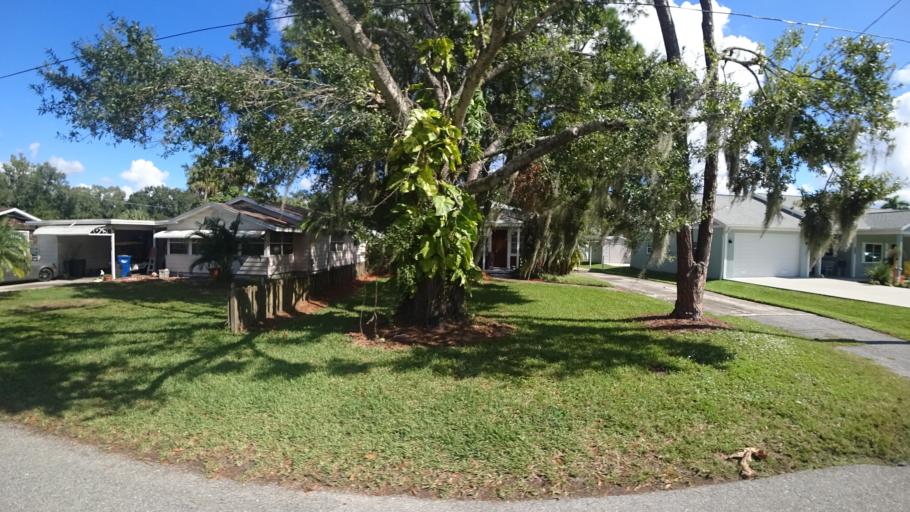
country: US
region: Florida
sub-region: Manatee County
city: Ellenton
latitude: 27.5194
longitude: -82.5301
